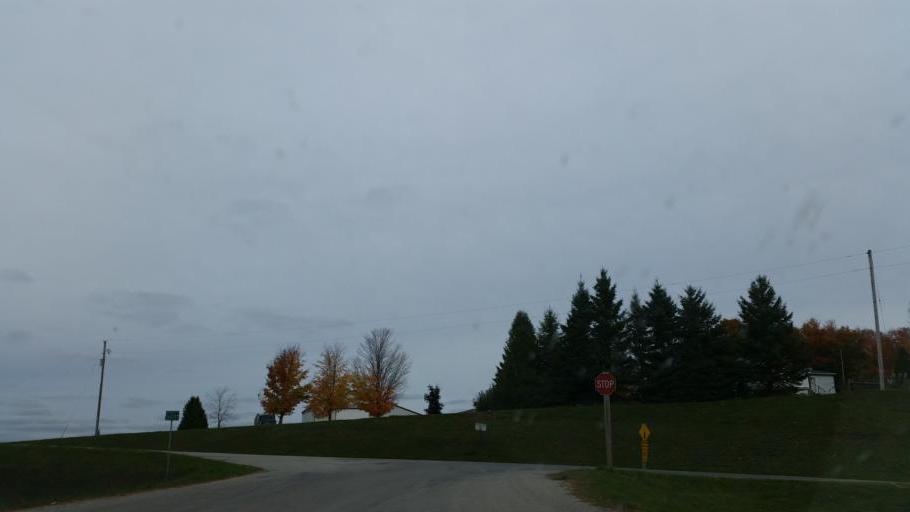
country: CA
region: Ontario
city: Wingham
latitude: 43.9766
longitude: -81.3320
